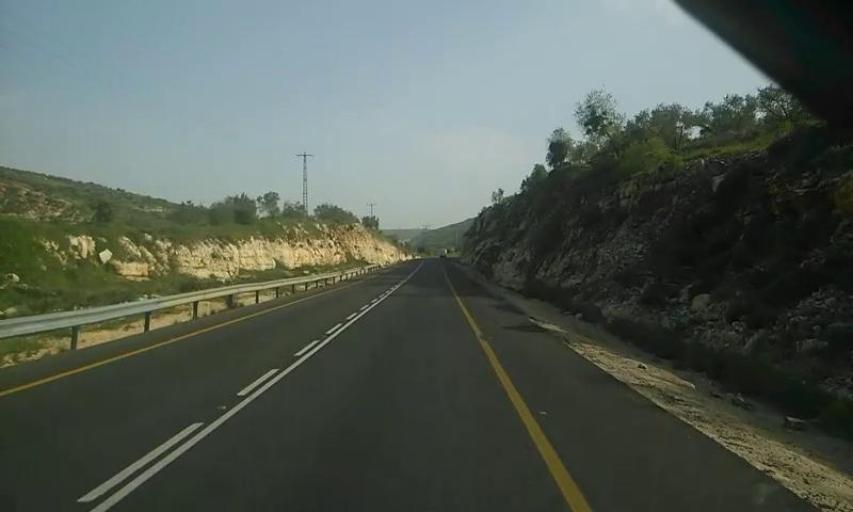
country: PS
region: West Bank
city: Jit
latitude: 32.2218
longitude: 35.1742
